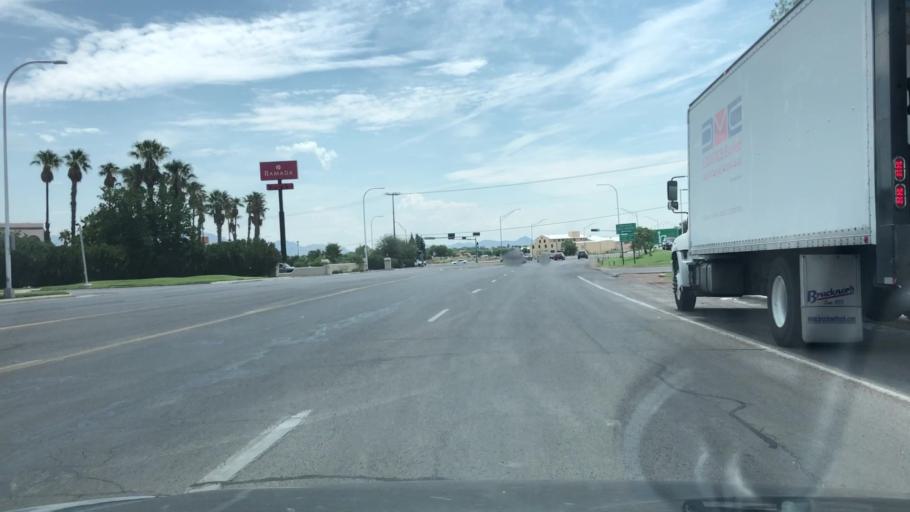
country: US
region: New Mexico
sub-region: Dona Ana County
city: University Park
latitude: 32.2827
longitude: -106.7695
